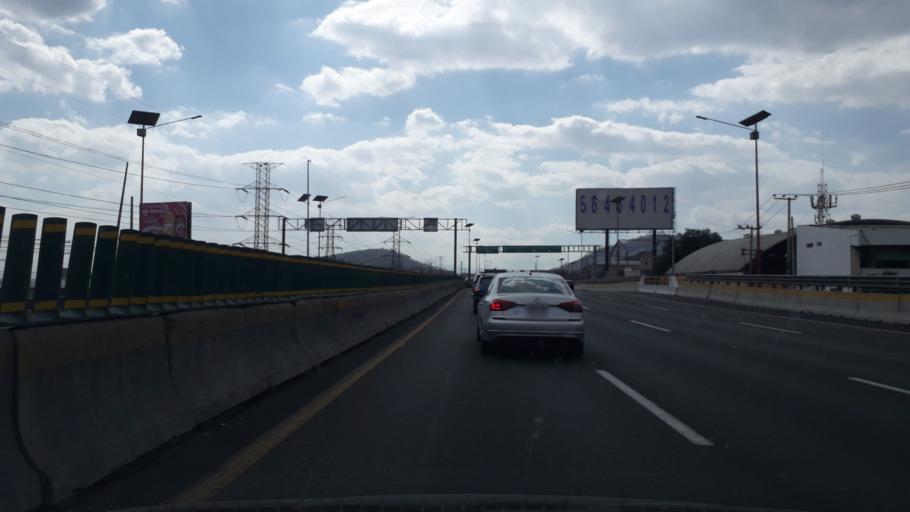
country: MX
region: Mexico
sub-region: Tlalnepantla de Baz
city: Puerto Escondido (Tepeolulco Puerto Escondido)
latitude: 19.5273
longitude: -99.0845
